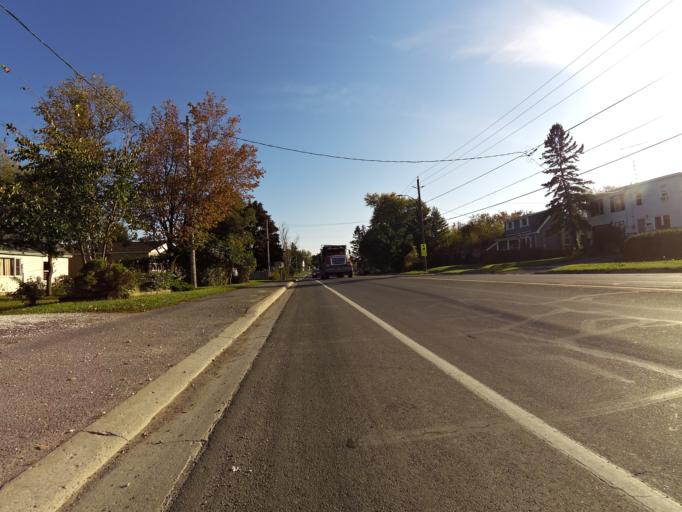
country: CA
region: Ontario
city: Kingston
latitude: 44.2668
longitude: -76.4787
